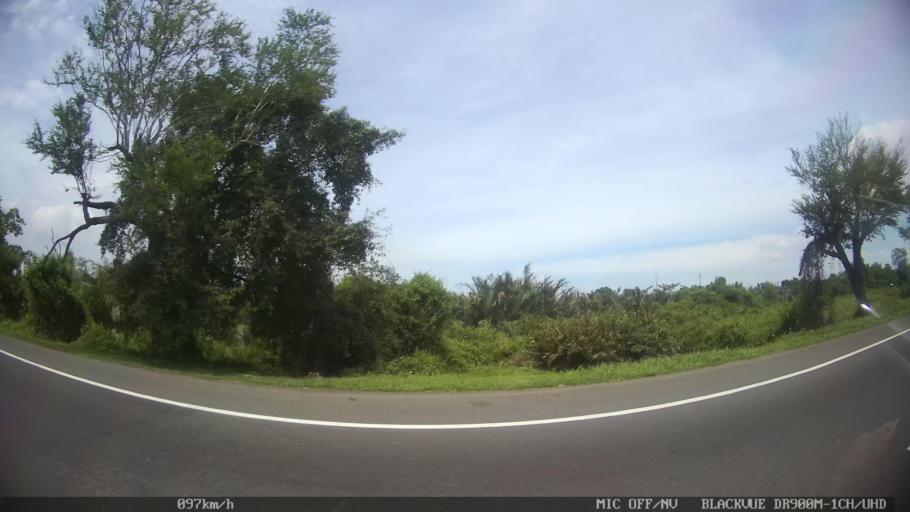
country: ID
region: North Sumatra
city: Labuhan Deli
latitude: 3.7436
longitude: 98.6795
